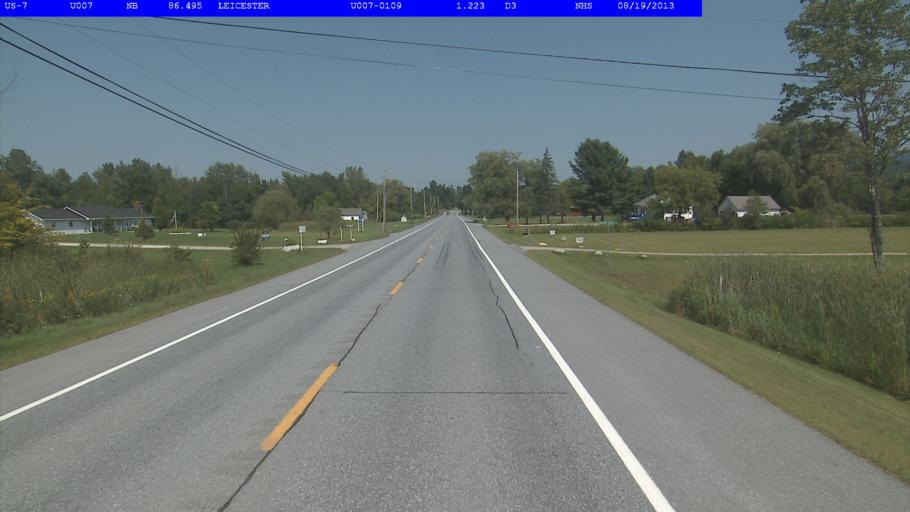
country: US
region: Vermont
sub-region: Rutland County
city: Brandon
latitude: 43.8609
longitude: -73.1067
